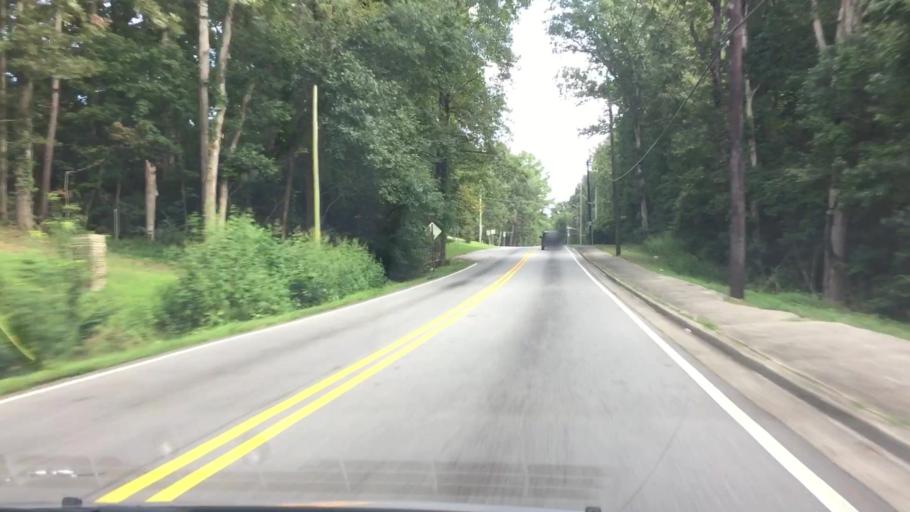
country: US
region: Georgia
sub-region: Clayton County
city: Conley
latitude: 33.6716
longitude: -84.3086
